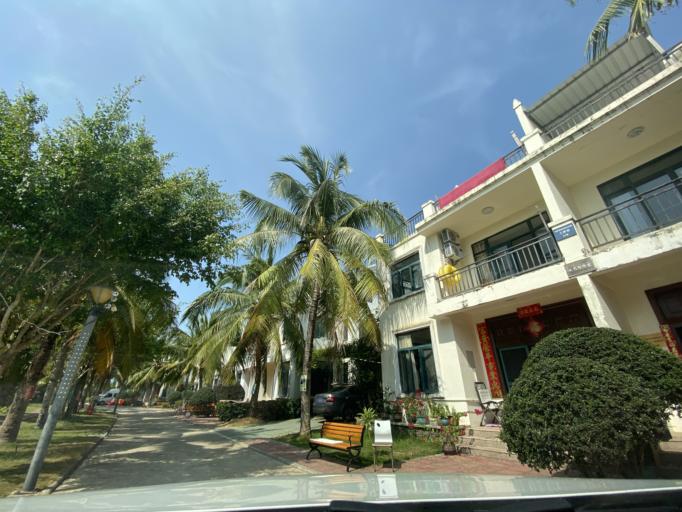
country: CN
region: Hainan
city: Yingzhou
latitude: 18.4107
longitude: 109.8325
